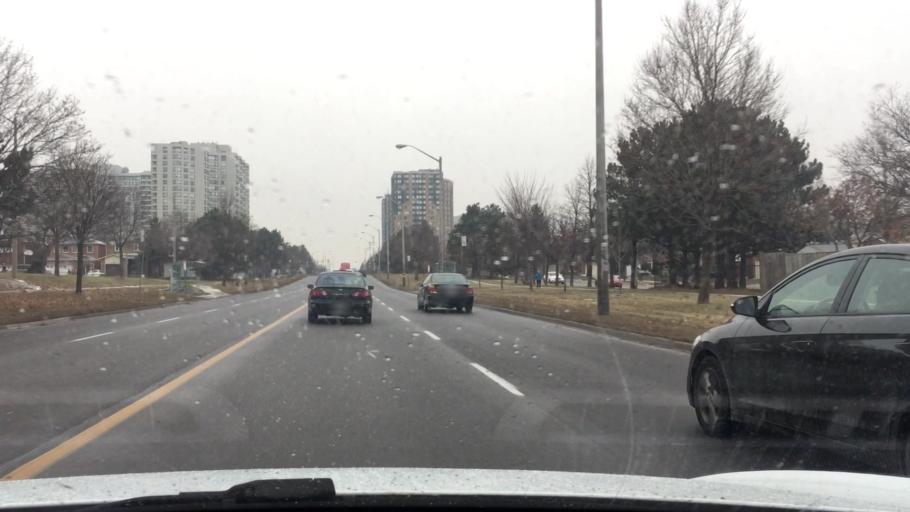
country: CA
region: Ontario
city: Markham
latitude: 43.8195
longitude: -79.2726
